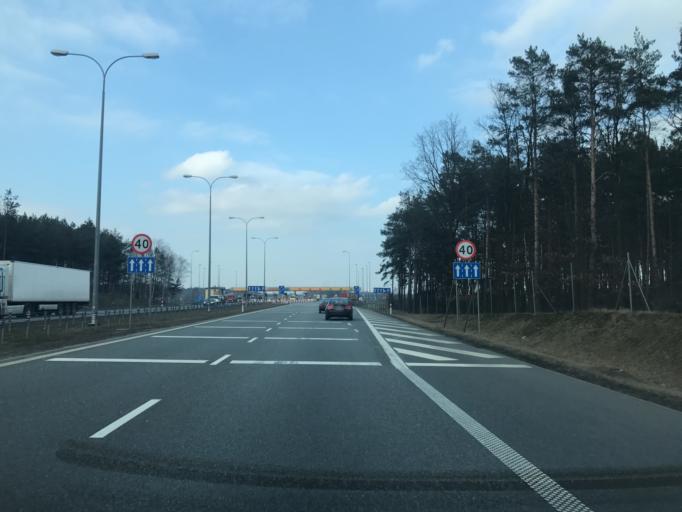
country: PL
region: Kujawsko-Pomorskie
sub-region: Powiat torunski
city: Lubicz Dolny
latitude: 53.0074
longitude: 18.7338
